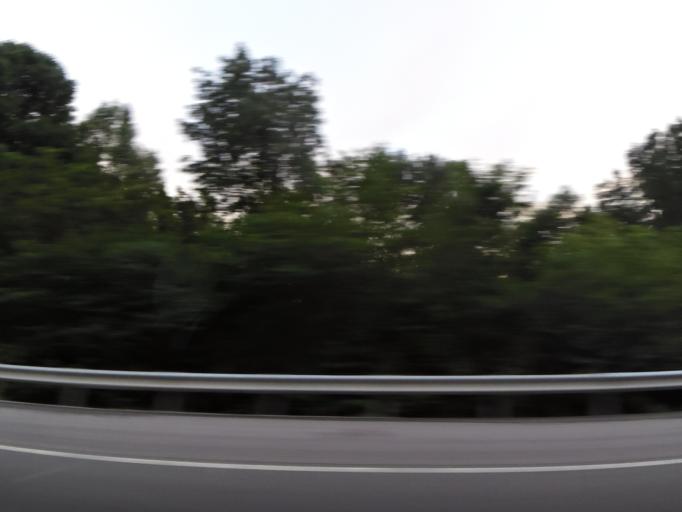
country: US
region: Tennessee
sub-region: Putnam County
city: Monterey
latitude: 36.1295
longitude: -85.3543
